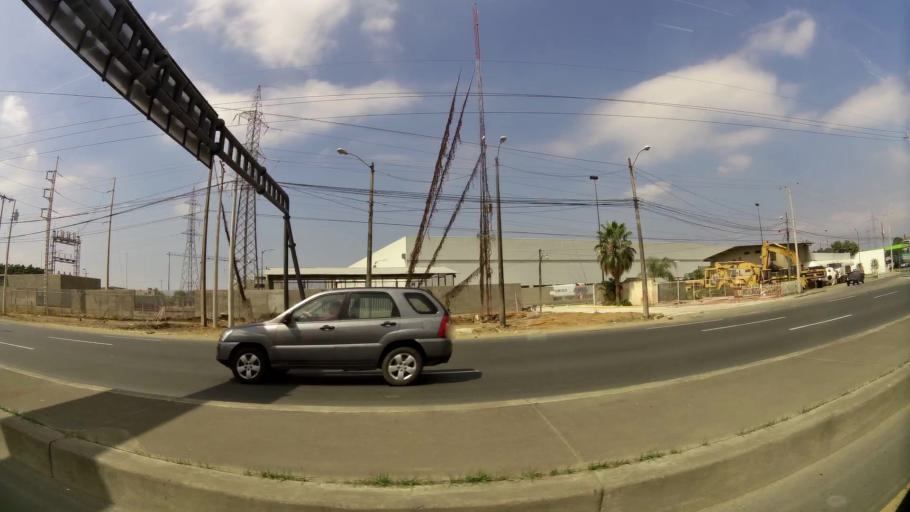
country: EC
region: Guayas
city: Eloy Alfaro
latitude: -2.0645
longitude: -79.9251
